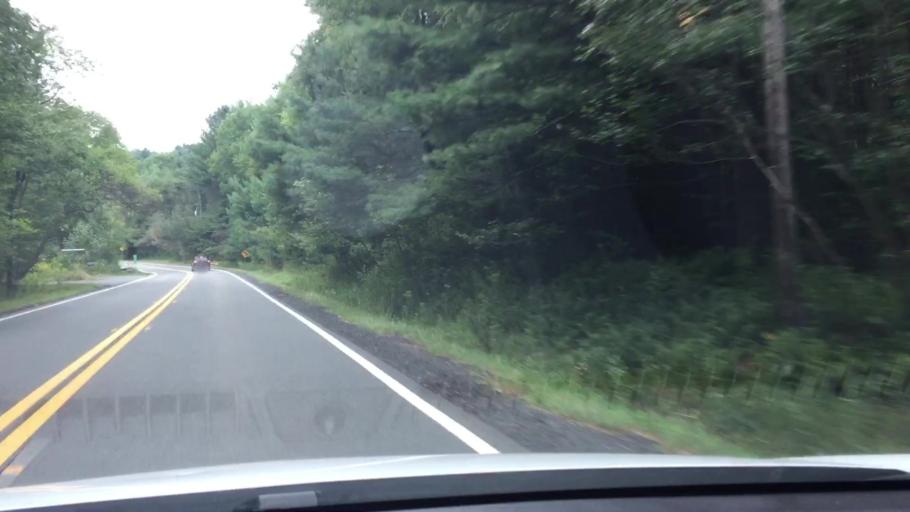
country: US
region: Massachusetts
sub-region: Berkshire County
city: Becket
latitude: 42.3471
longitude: -73.0925
